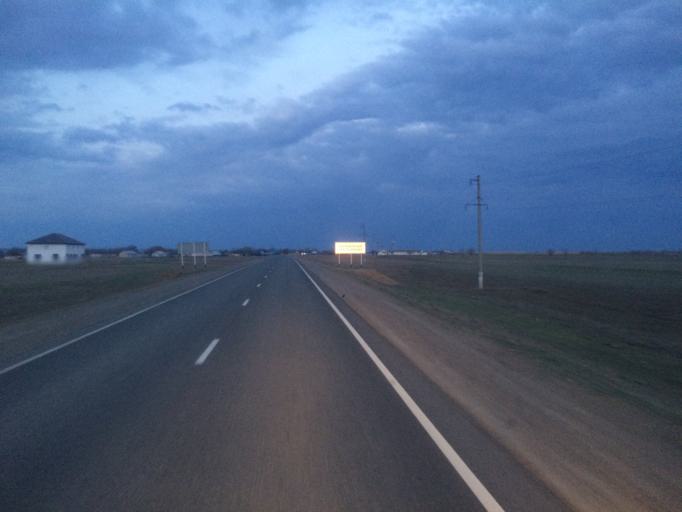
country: KZ
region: Aqtoebe
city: Martuk
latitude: 50.6402
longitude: 56.6821
